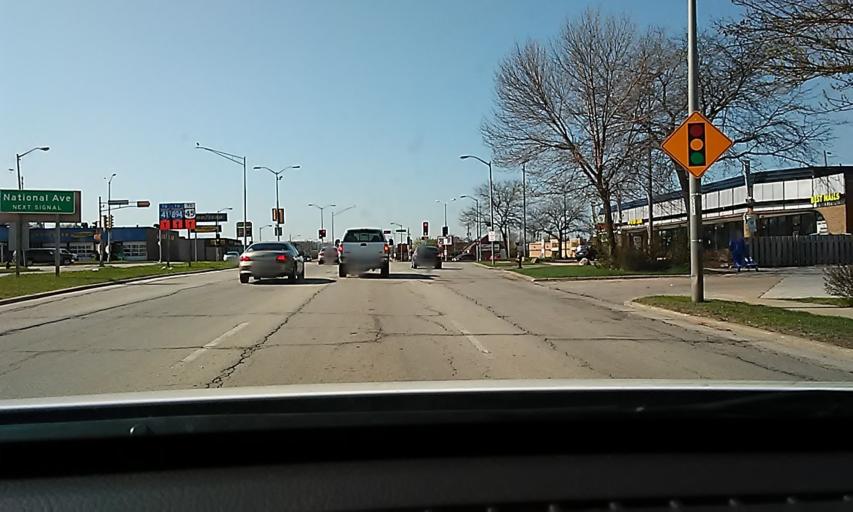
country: US
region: Wisconsin
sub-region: Milwaukee County
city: West Allis
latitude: 42.9946
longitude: -88.0471
